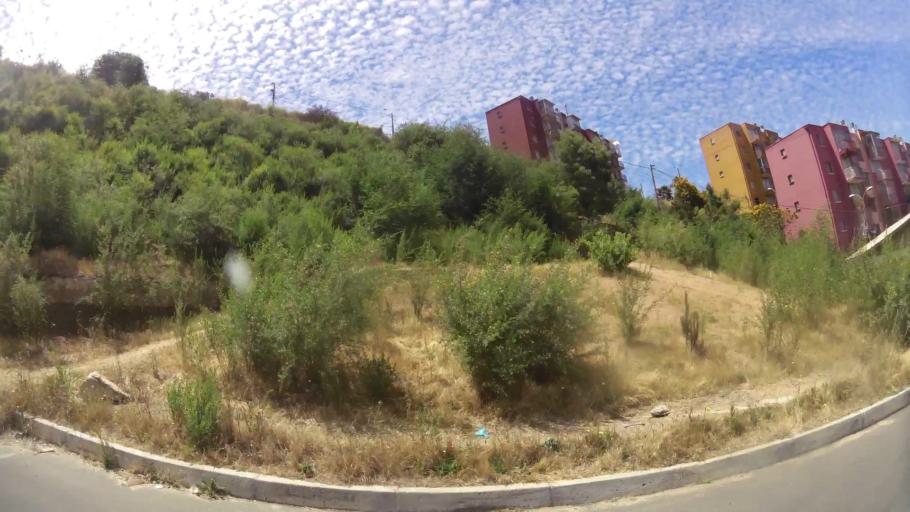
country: CL
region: Valparaiso
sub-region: Provincia de Valparaiso
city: Vina del Mar
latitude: -33.0601
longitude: -71.5612
